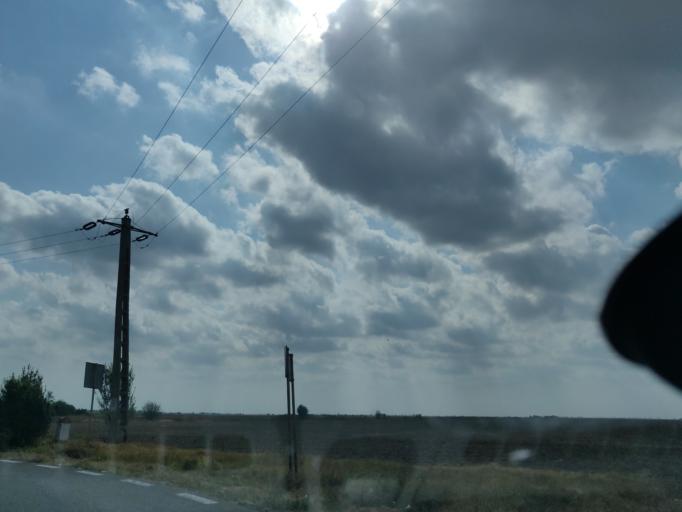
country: RO
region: Vrancea
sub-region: Comuna Ciorasti
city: Ciorasti
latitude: 45.4279
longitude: 27.3011
